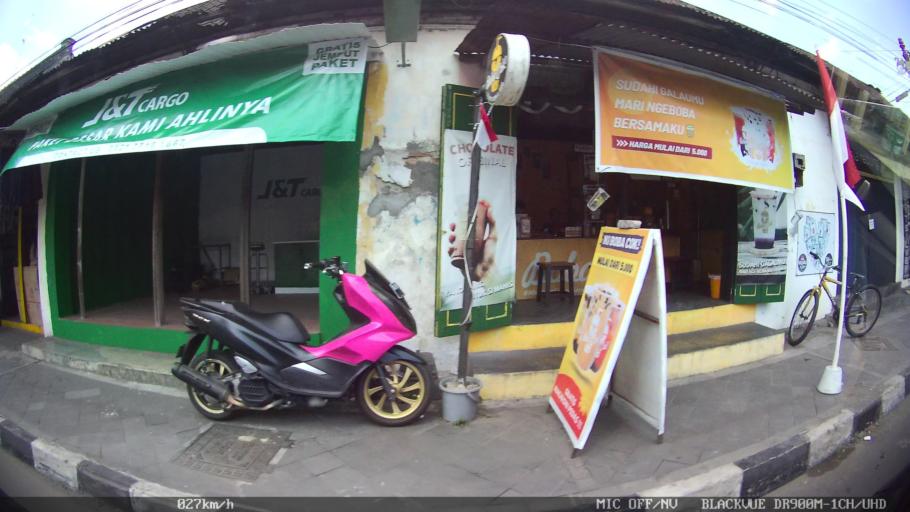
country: ID
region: Daerah Istimewa Yogyakarta
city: Yogyakarta
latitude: -7.8242
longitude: 110.4005
